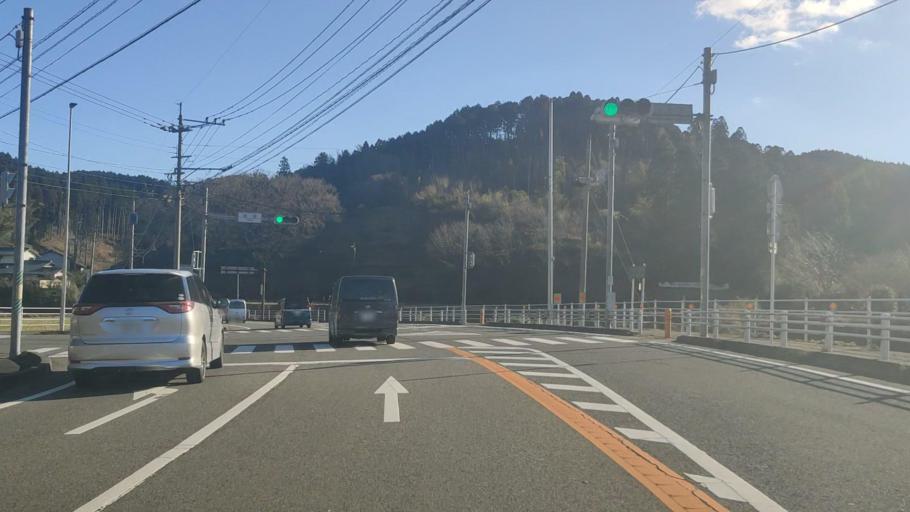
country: JP
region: Saga Prefecture
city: Kanzakimachi-kanzaki
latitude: 33.4225
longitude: 130.2773
